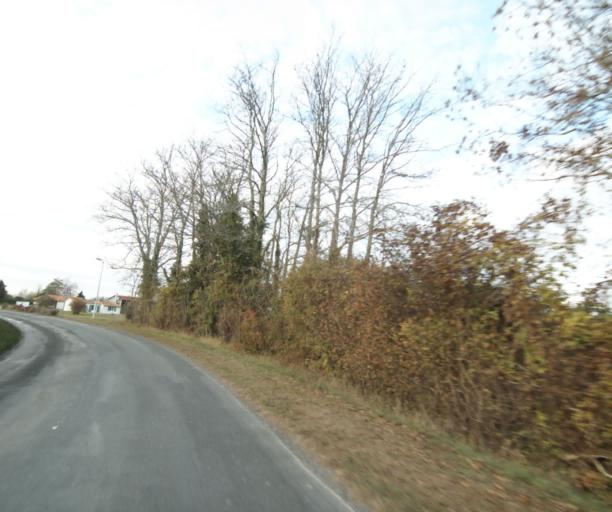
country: FR
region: Poitou-Charentes
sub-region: Departement de la Charente-Maritime
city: Les Gonds
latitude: 45.7117
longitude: -0.6033
